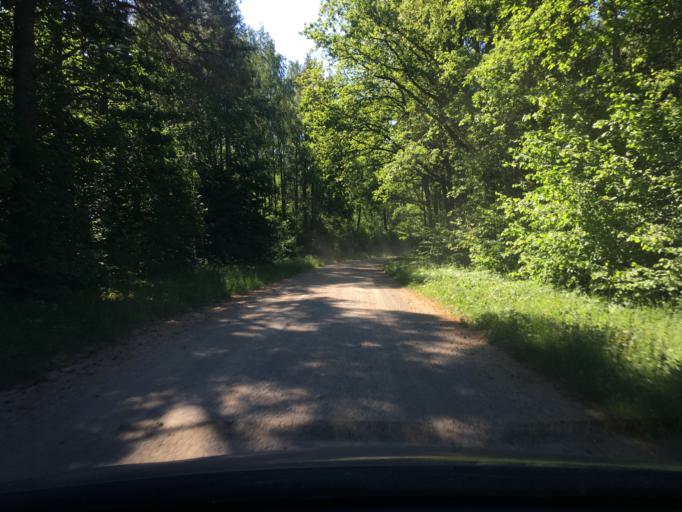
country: EE
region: Laeaene
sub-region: Lihula vald
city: Lihula
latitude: 58.6435
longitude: 23.7871
